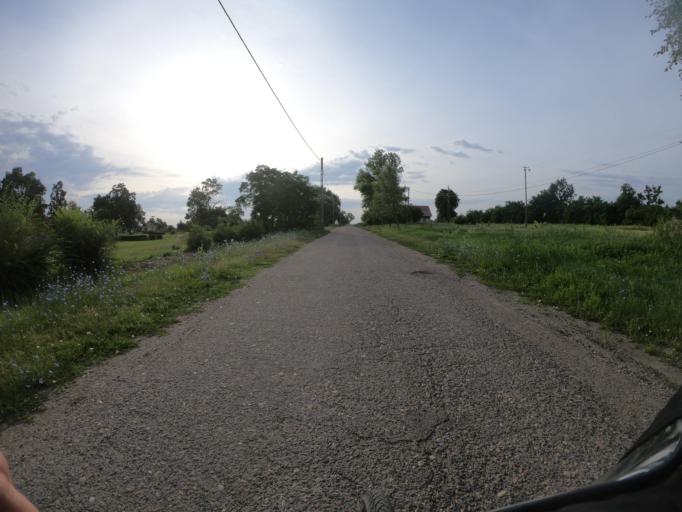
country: HU
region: Hajdu-Bihar
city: Hortobagy
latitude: 47.6046
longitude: 21.0729
